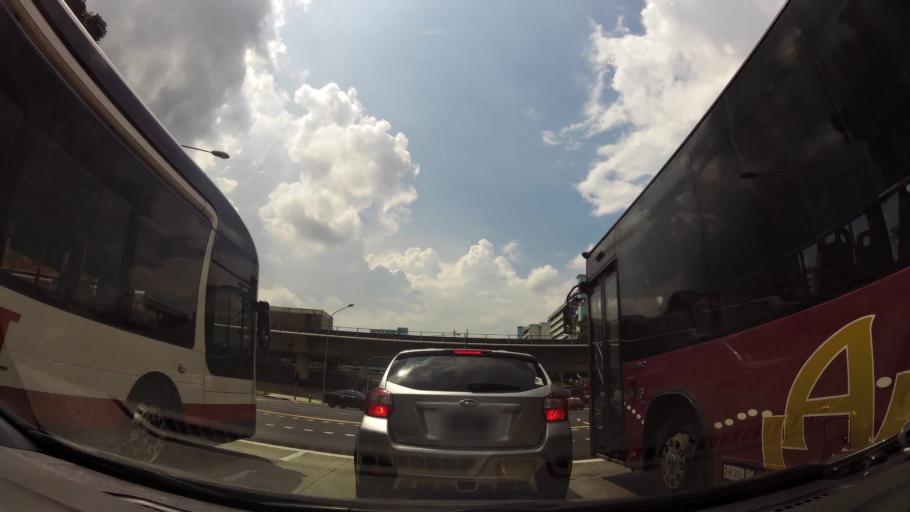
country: MY
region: Johor
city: Kampung Pasir Gudang Baru
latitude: 1.4303
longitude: 103.8356
